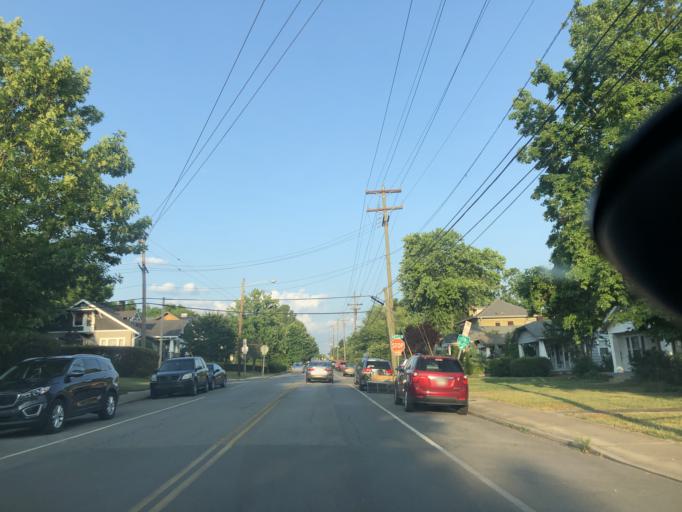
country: US
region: Tennessee
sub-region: Davidson County
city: Nashville
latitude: 36.1309
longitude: -86.8067
